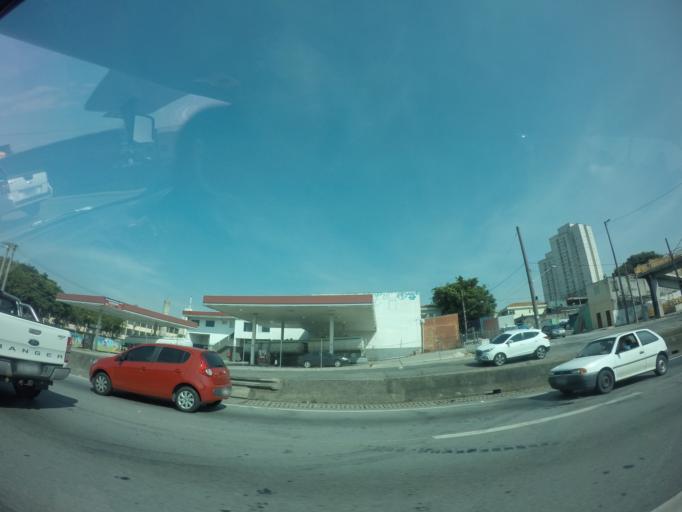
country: BR
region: Sao Paulo
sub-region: Guarulhos
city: Guarulhos
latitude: -23.5106
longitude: -46.5746
